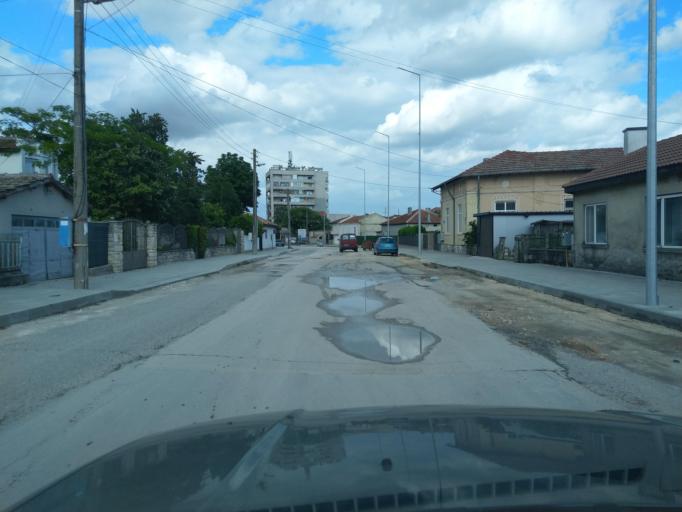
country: BG
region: Dobrich
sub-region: Obshtina Kavarna
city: Kavarna
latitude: 43.4301
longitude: 28.3340
